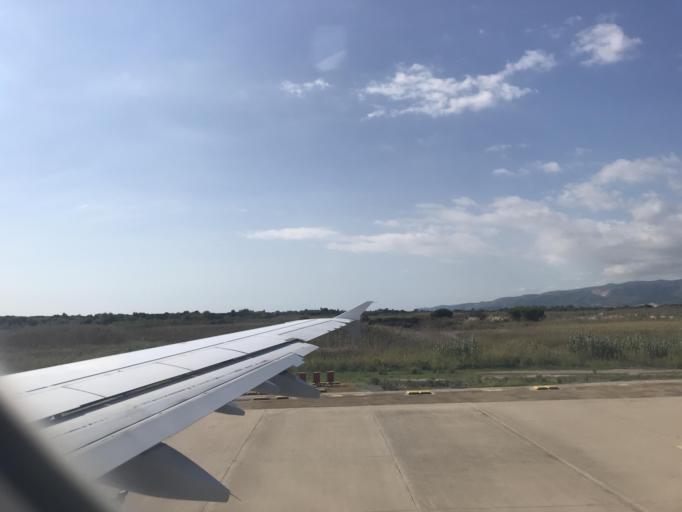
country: ES
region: Catalonia
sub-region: Provincia de Barcelona
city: El Prat de Llobregat
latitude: 41.2831
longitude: 2.0734
